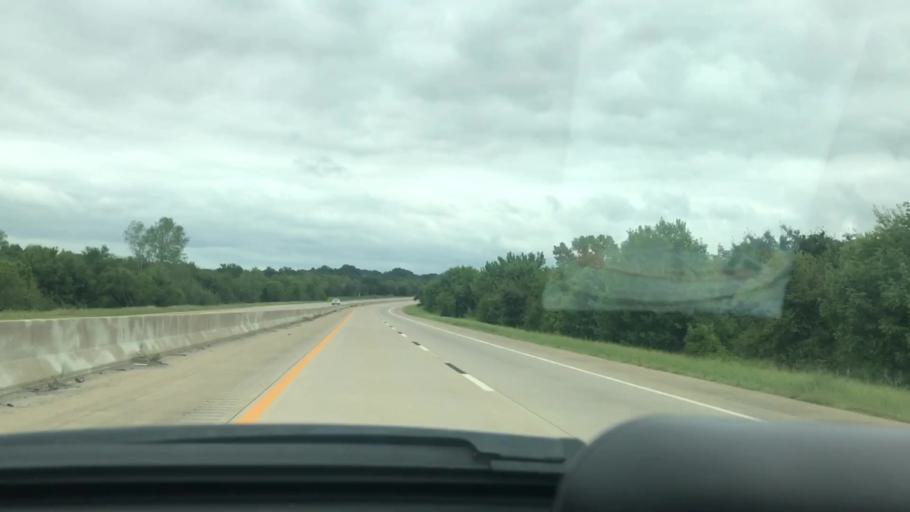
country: US
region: Oklahoma
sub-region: McIntosh County
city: Eufaula
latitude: 35.1892
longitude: -95.6391
